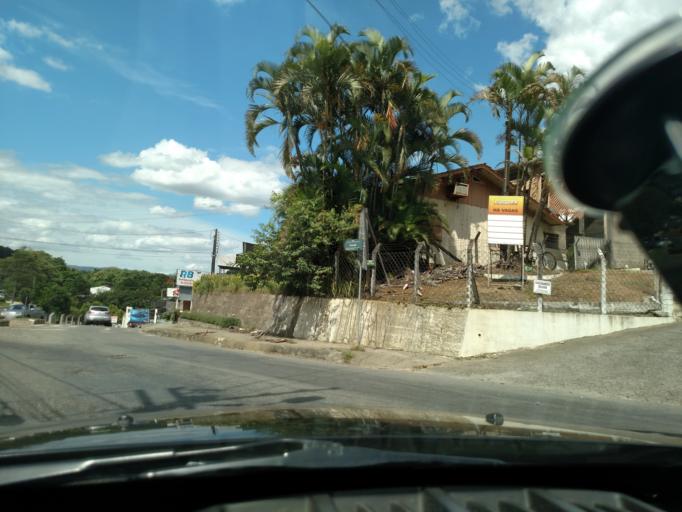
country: BR
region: Santa Catarina
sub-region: Blumenau
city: Blumenau
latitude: -26.8740
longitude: -49.1065
